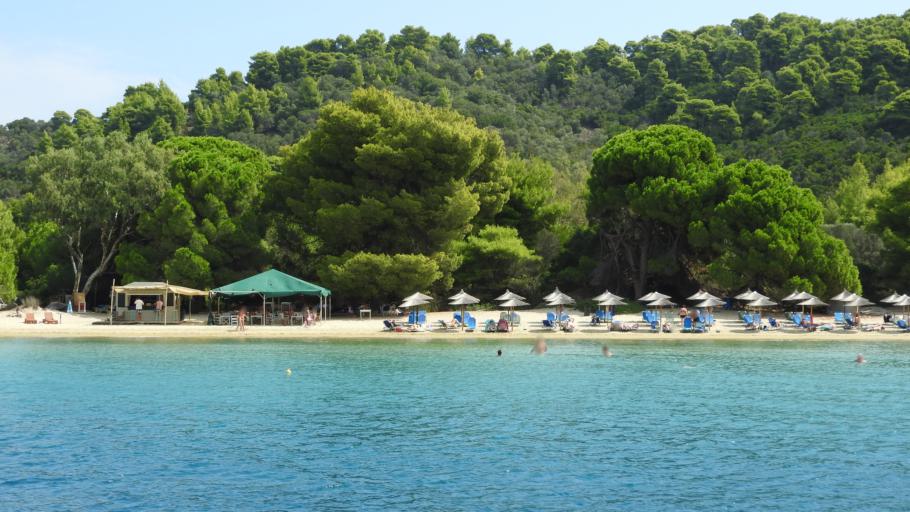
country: GR
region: Thessaly
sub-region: Nomos Magnisias
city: Skiathos
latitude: 39.1258
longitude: 23.4943
